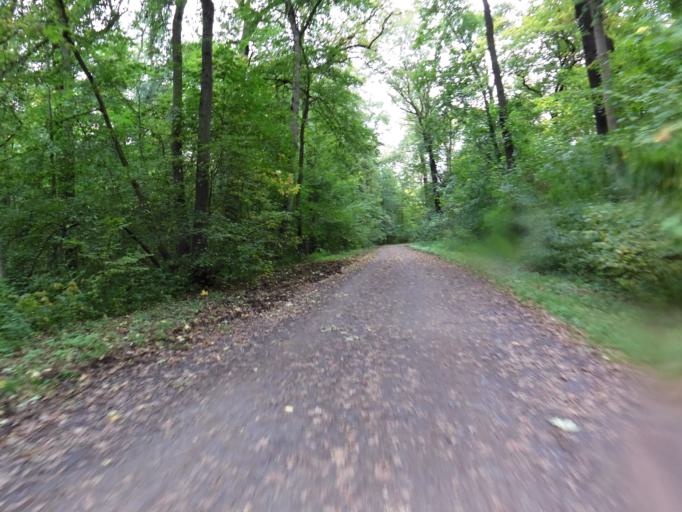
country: DE
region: Saxony
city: Markkleeberg
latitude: 51.2994
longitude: 12.3592
